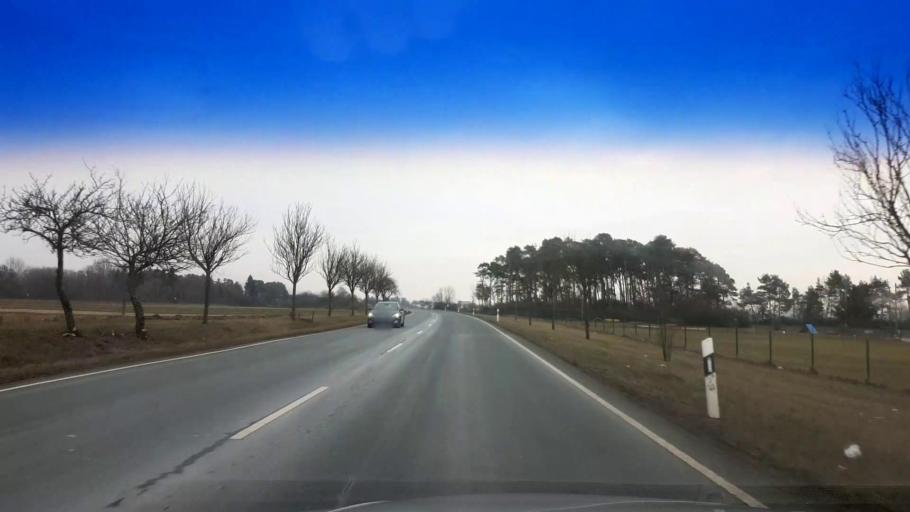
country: DE
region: Bavaria
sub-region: Upper Franconia
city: Hirschaid
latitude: 49.8096
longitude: 11.0000
